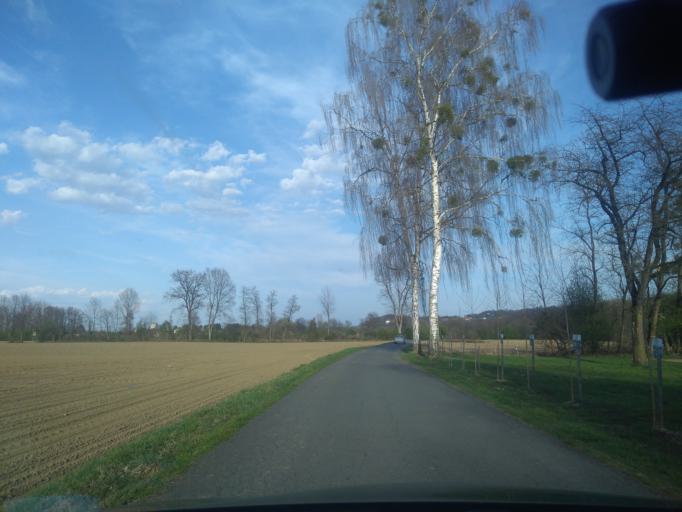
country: AT
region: Styria
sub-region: Politischer Bezirk Suedoststeiermark
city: Mureck
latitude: 46.7018
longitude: 15.7532
